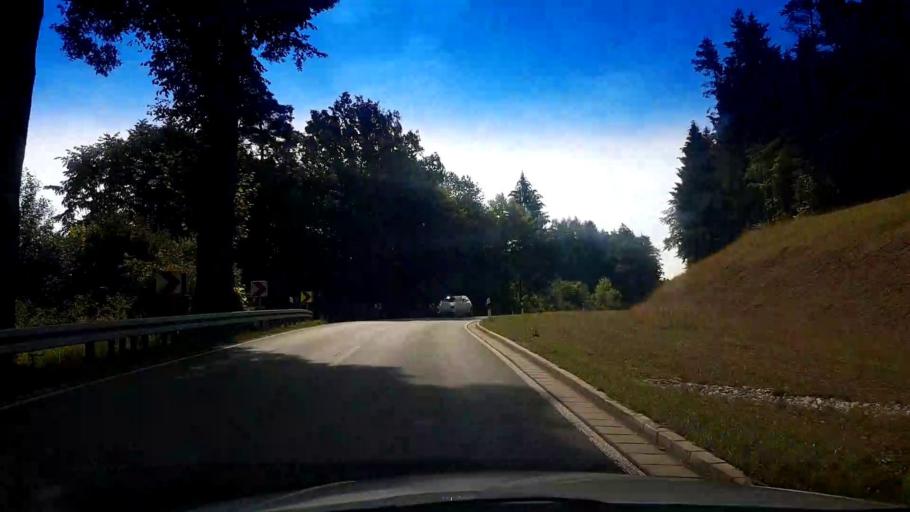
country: DE
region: Bavaria
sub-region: Upper Franconia
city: Plankenfels
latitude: 49.9373
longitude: 11.3734
